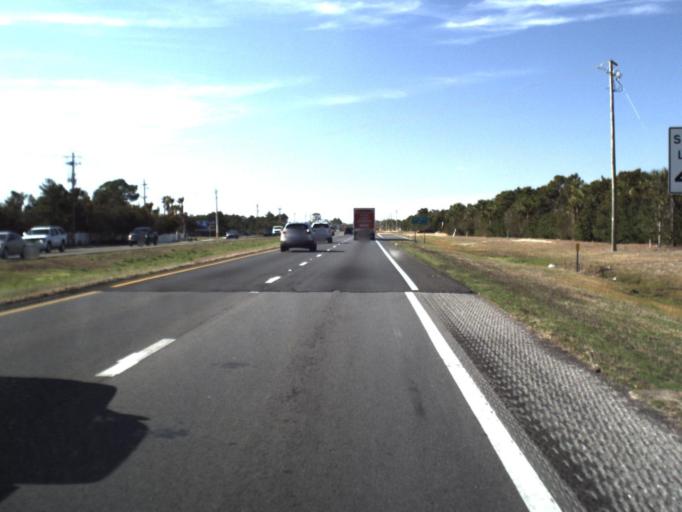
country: US
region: Florida
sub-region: Bay County
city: Panama City Beach
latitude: 30.2165
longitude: -85.8587
